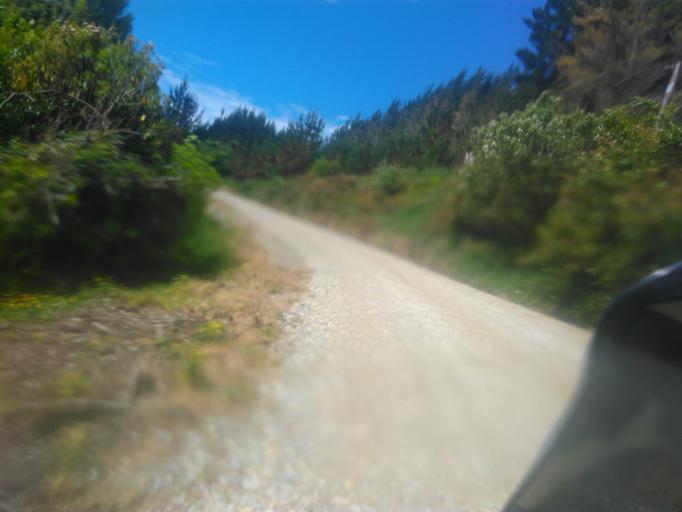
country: NZ
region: Hawke's Bay
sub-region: Wairoa District
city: Wairoa
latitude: -38.7711
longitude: 177.6000
